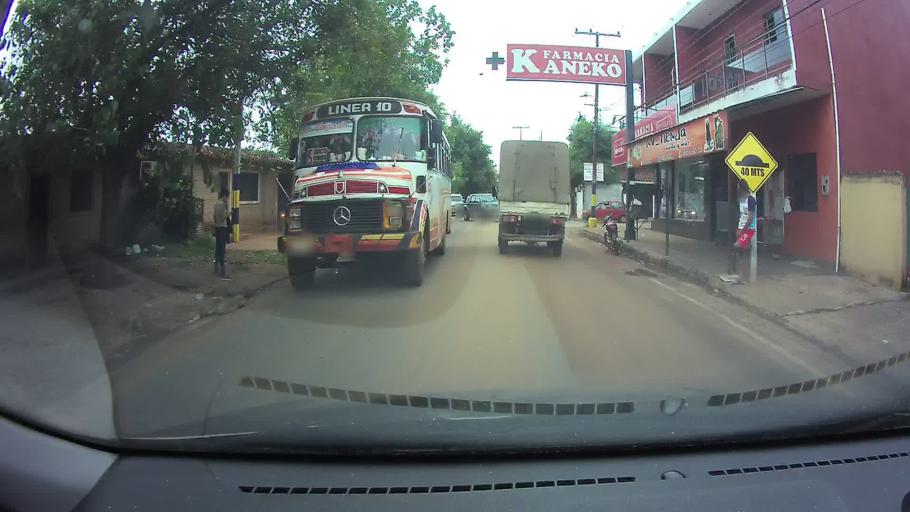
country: PY
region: Central
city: San Lorenzo
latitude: -25.3108
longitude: -57.4917
